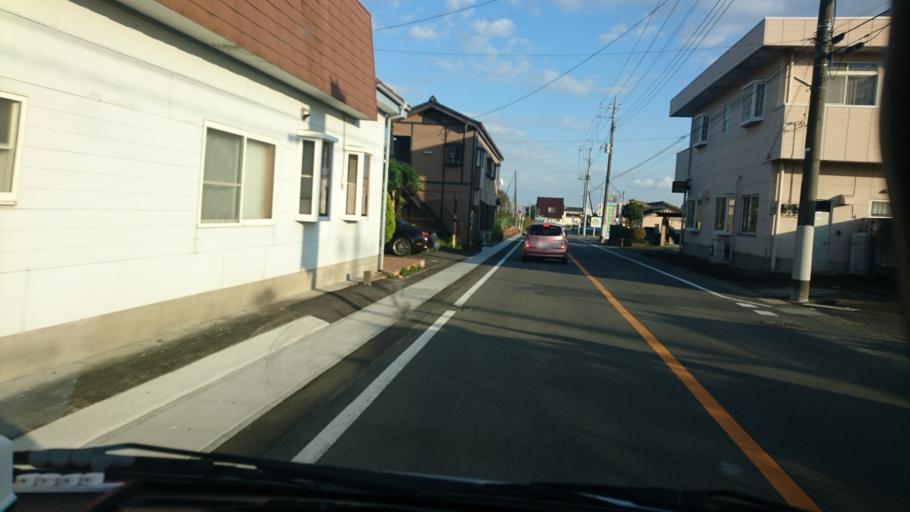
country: JP
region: Gunma
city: Omamacho-omama
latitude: 36.4200
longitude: 139.2965
